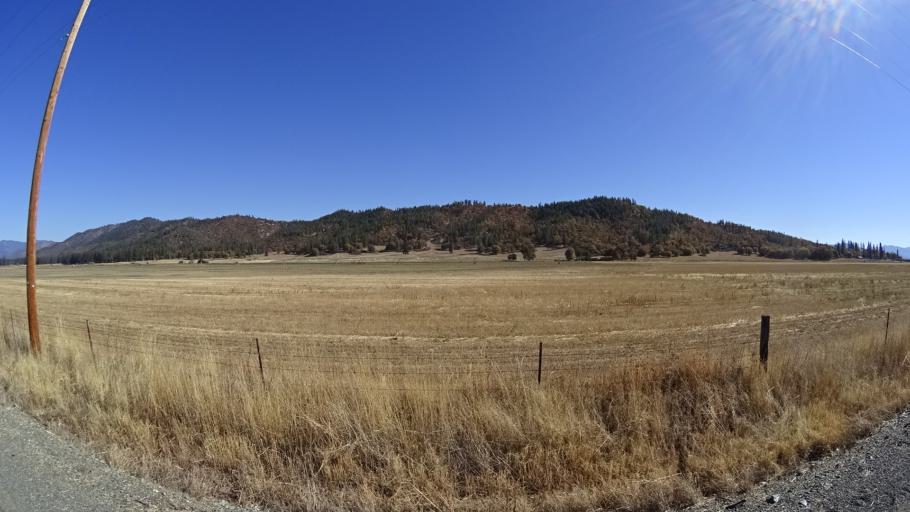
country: US
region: California
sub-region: Siskiyou County
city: Yreka
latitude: 41.5627
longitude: -122.9232
